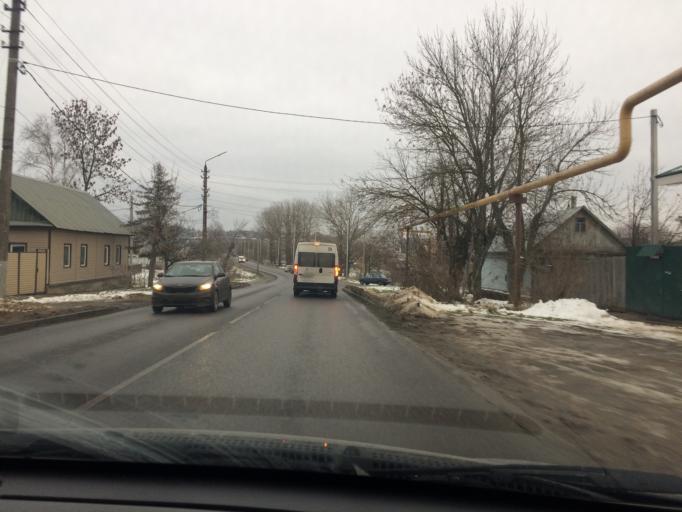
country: RU
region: Tula
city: Gorelki
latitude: 54.2382
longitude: 37.6448
